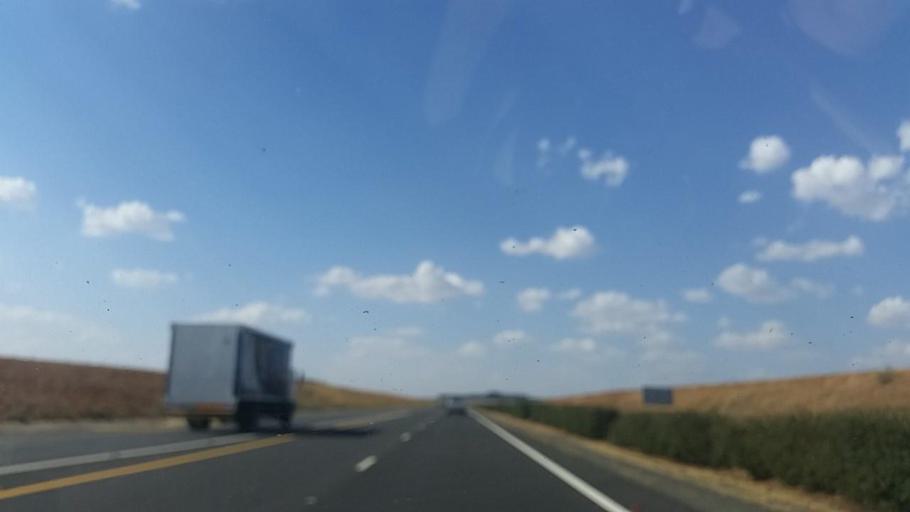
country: ZA
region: Orange Free State
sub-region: Mangaung Metropolitan Municipality
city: Bloemfontein
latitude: -29.1984
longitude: 26.1916
